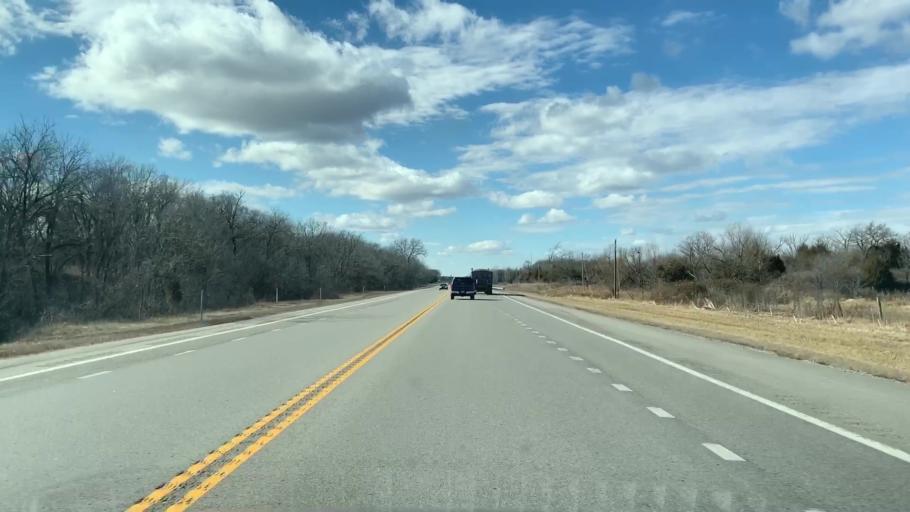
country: US
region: Kansas
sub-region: Cherokee County
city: Columbus
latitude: 37.3400
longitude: -94.9273
